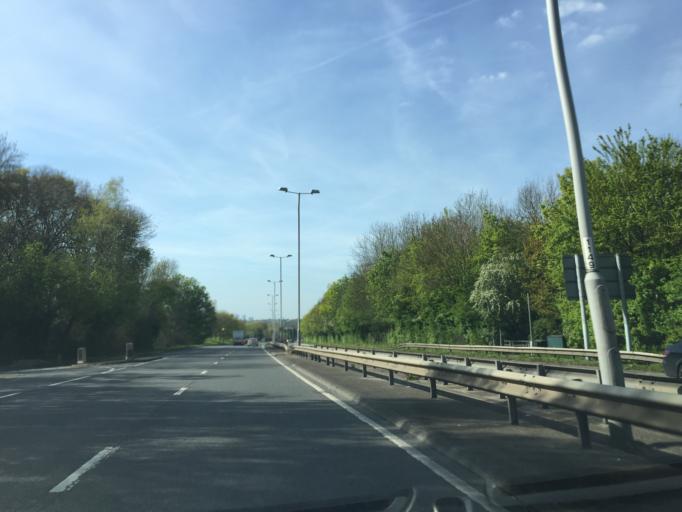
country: GB
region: England
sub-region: Greater London
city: Sidcup
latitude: 51.4238
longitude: 0.0898
